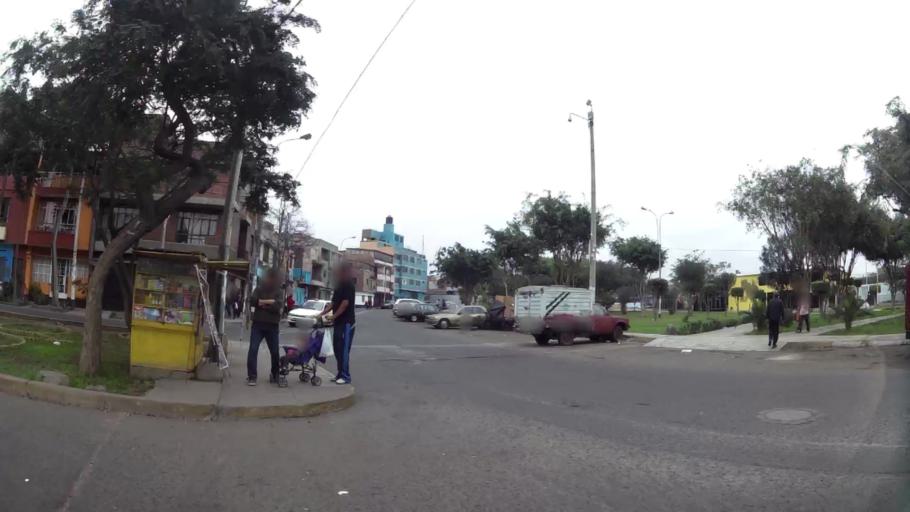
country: PE
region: Lima
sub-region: Lima
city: San Luis
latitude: -12.0765
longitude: -77.0227
